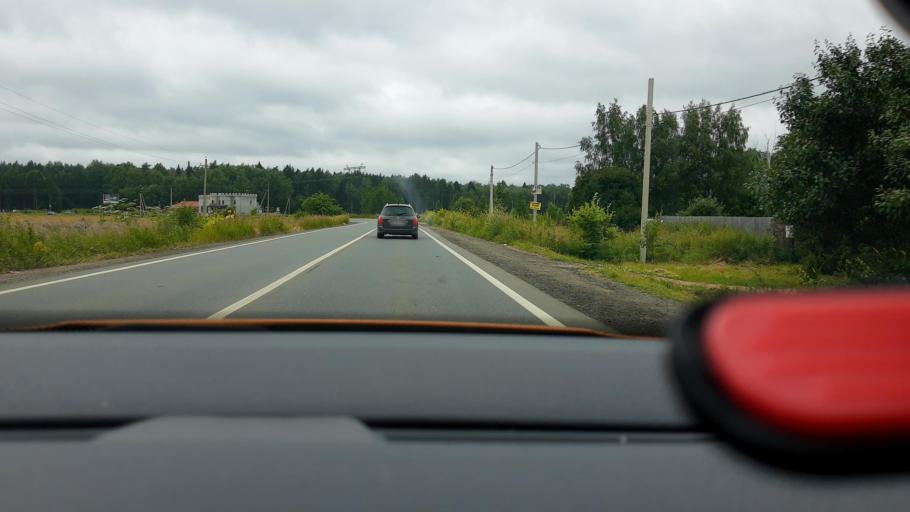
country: RU
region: Moskovskaya
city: Pirogovskiy
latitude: 55.9990
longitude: 37.7052
